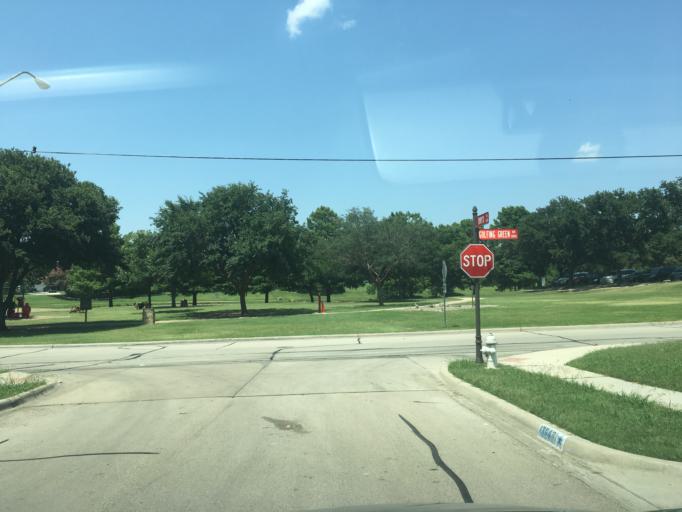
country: US
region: Texas
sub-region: Dallas County
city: Farmers Branch
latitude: 32.9313
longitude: -96.8747
